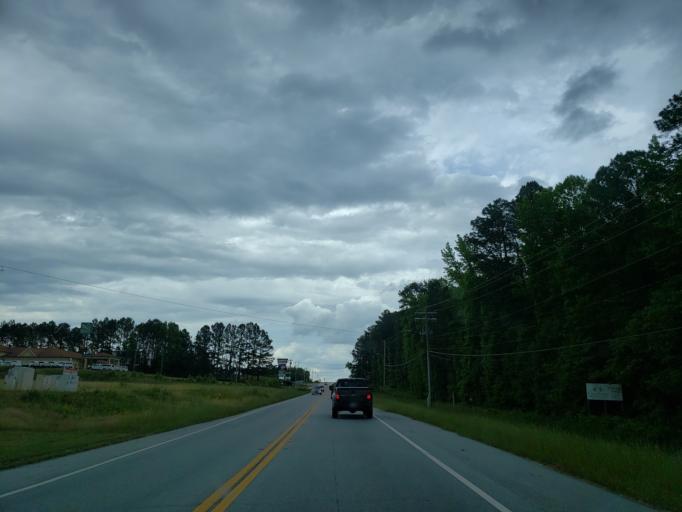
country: US
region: Georgia
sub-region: Haralson County
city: Bremen
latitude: 33.6935
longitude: -85.1467
